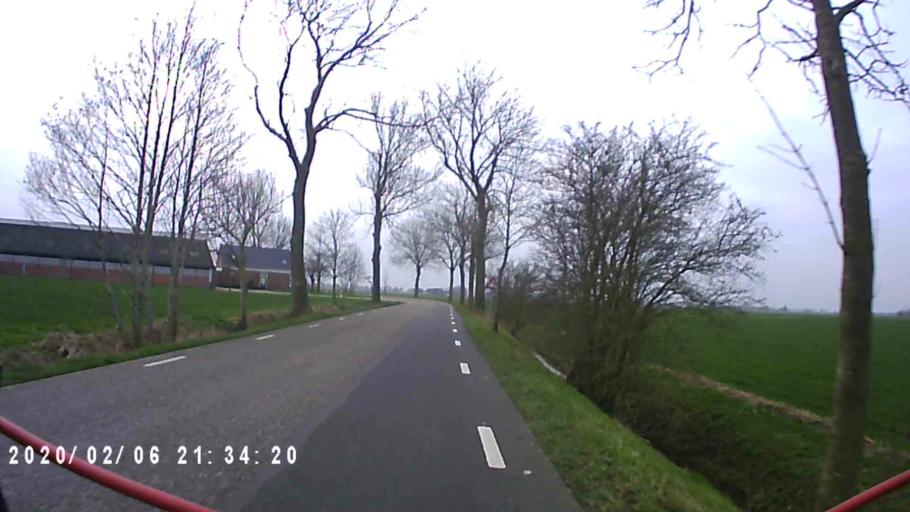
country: NL
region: Groningen
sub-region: Gemeente Zuidhorn
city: Noordhorn
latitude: 53.2737
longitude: 6.3904
